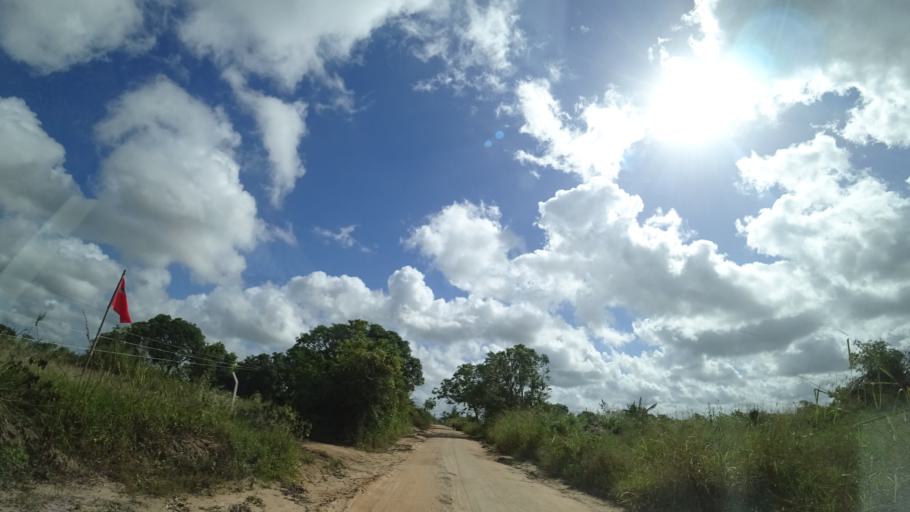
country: MZ
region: Sofala
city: Dondo
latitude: -19.3999
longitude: 34.7090
